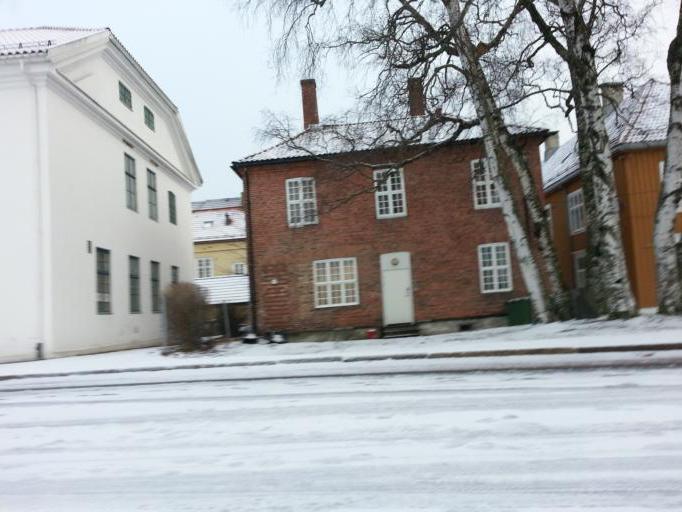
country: NO
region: Sor-Trondelag
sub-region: Trondheim
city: Trondheim
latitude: 63.4297
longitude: 10.3787
